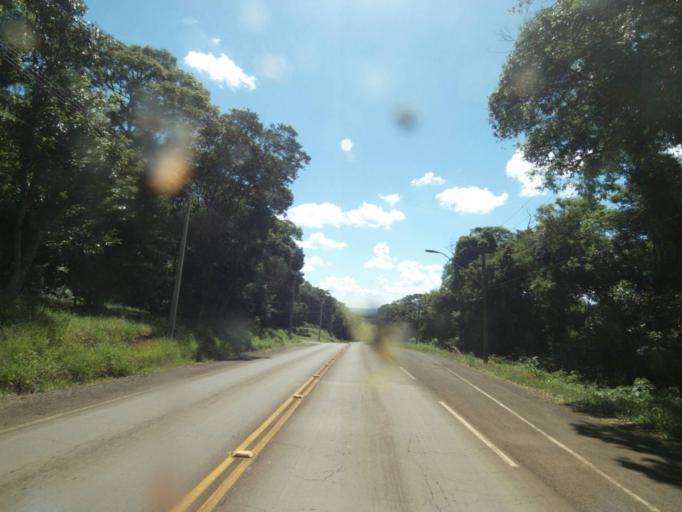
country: BR
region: Parana
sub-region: Chopinzinho
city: Chopinzinho
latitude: -25.7912
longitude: -52.0904
